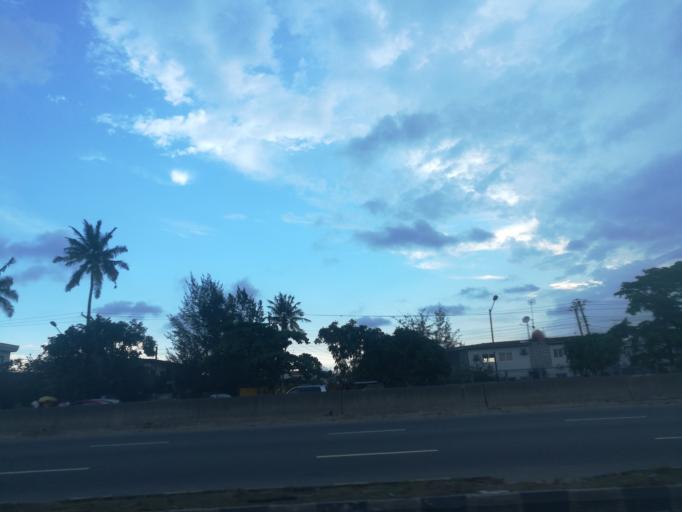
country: NG
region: Lagos
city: Somolu
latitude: 6.5512
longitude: 3.3765
